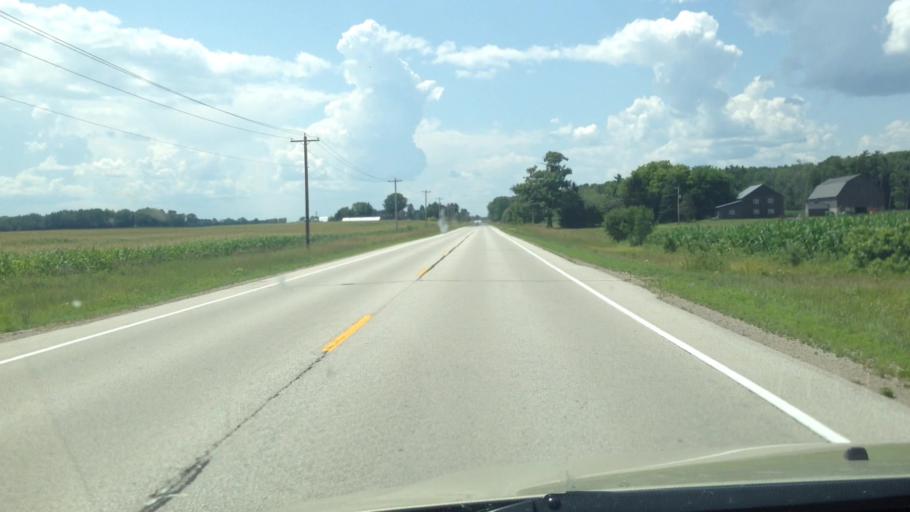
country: US
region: Wisconsin
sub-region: Brown County
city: Pulaski
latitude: 44.6587
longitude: -88.1908
